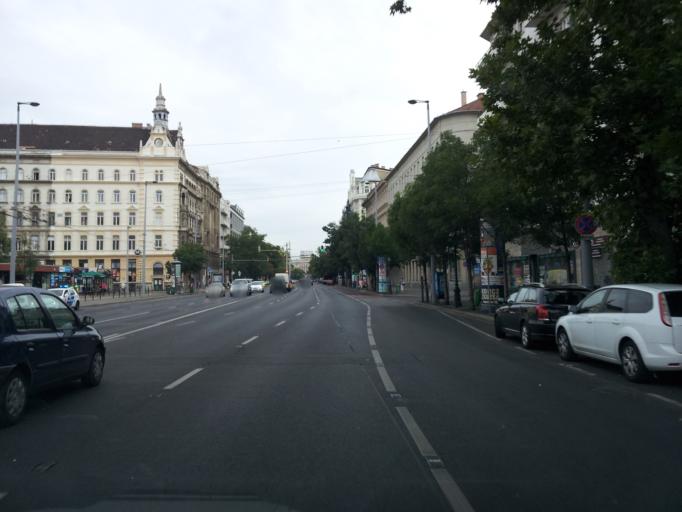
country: HU
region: Budapest
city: Budapest VI. keruelet
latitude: 47.5025
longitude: 19.0549
